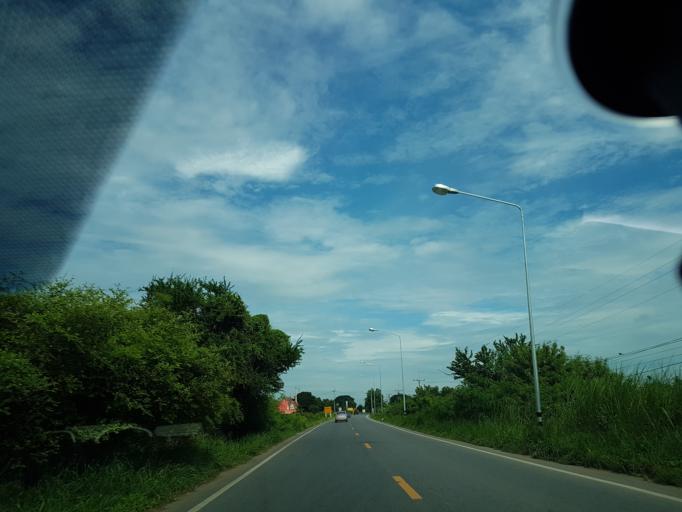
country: TH
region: Ang Thong
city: Chaiyo
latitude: 14.7228
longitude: 100.4847
